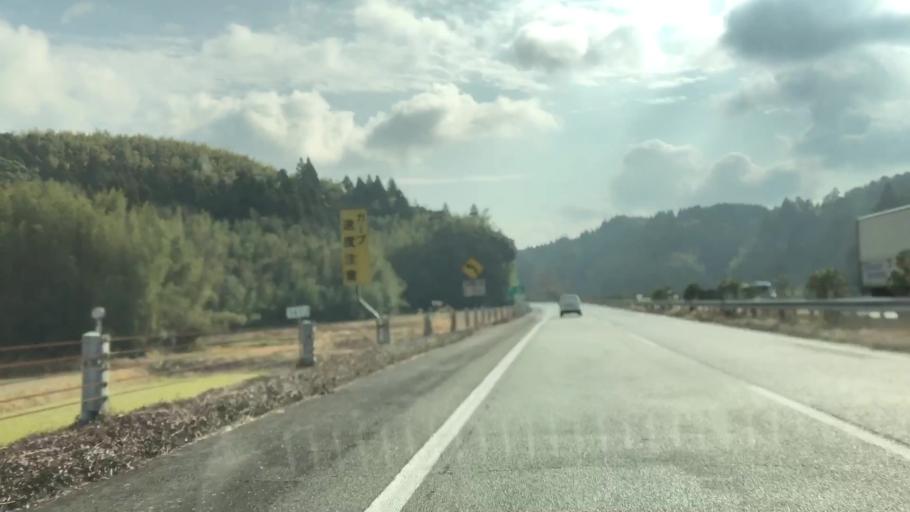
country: JP
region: Kumamoto
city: Yamaga
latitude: 33.0265
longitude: 130.5770
